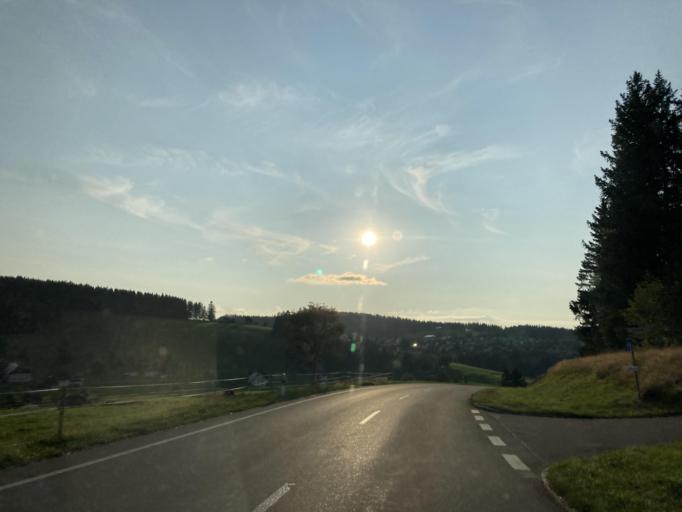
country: DE
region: Baden-Wuerttemberg
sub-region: Freiburg Region
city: Schonwald im Schwarzwald
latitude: 48.1017
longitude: 8.2188
